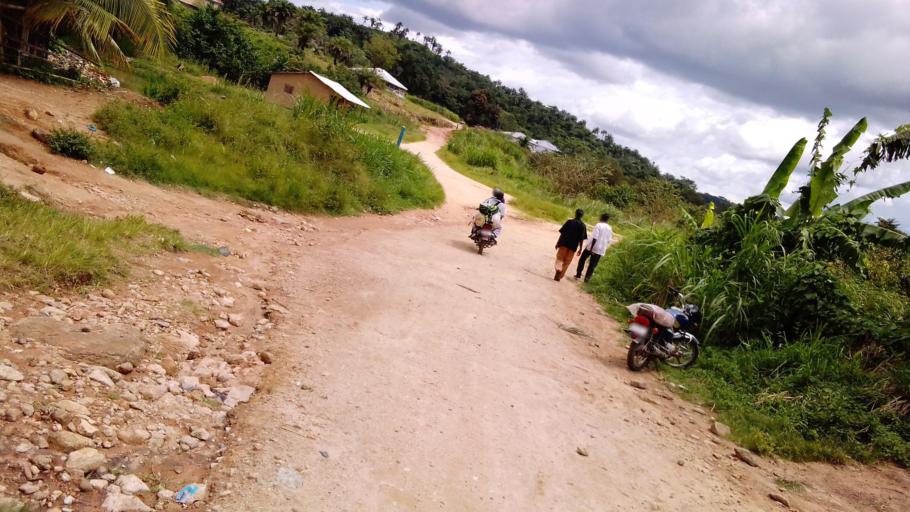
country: SL
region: Eastern Province
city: Koyima
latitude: 8.6997
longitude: -11.0121
